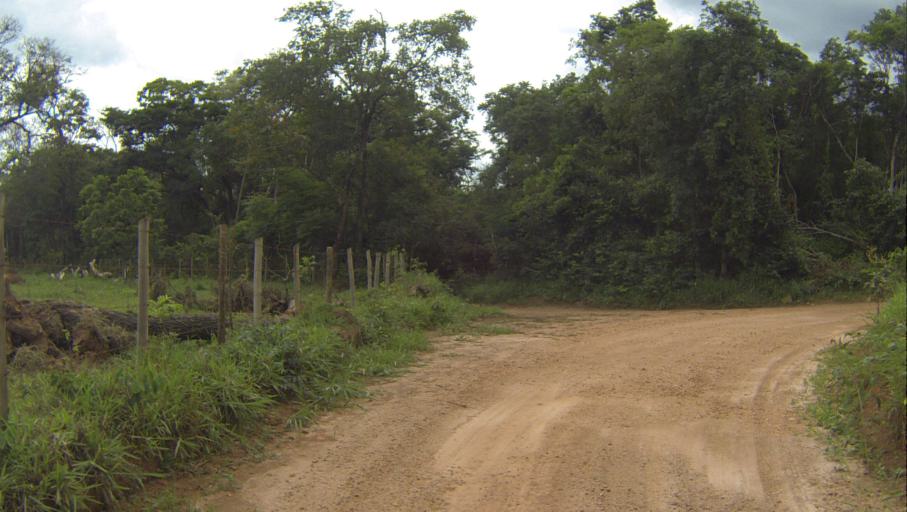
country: BR
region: Minas Gerais
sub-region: Brumadinho
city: Brumadinho
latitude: -20.1676
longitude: -44.1250
